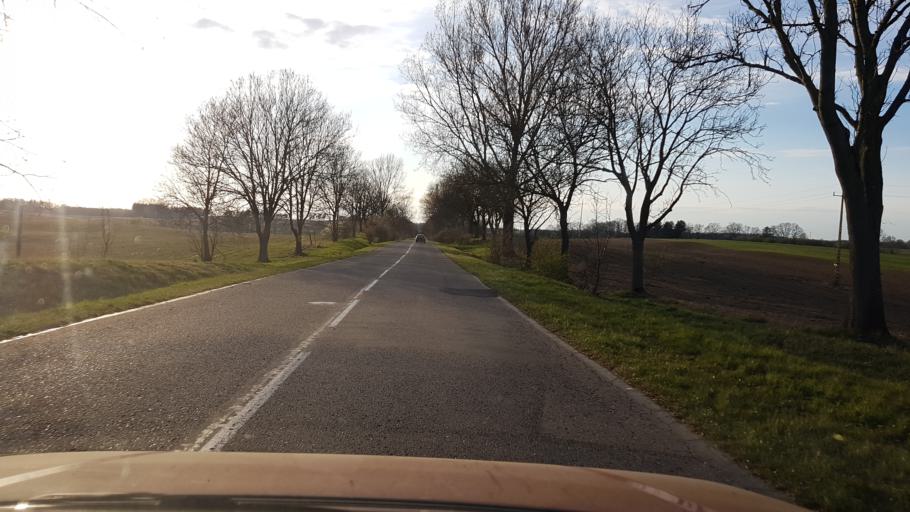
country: PL
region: West Pomeranian Voivodeship
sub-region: Powiat stargardzki
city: Insko
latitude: 53.4537
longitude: 15.4585
